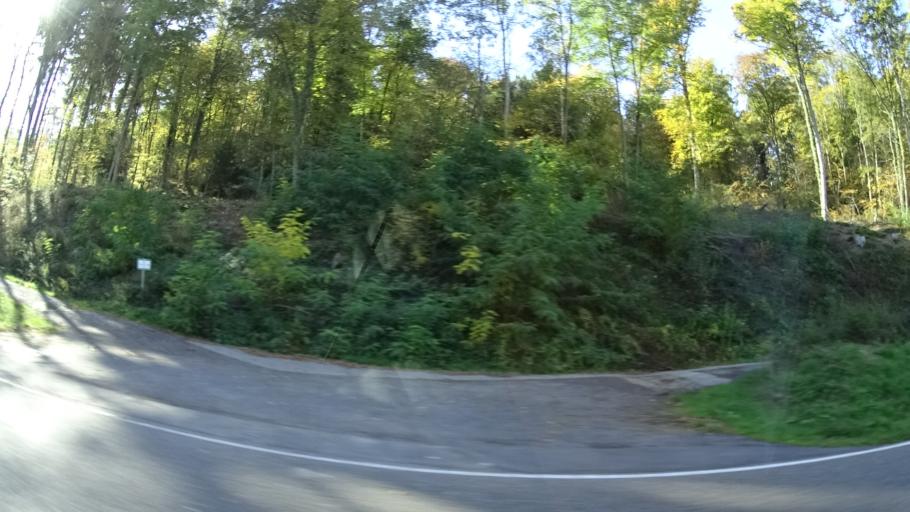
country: DE
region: Baden-Wuerttemberg
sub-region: Karlsruhe Region
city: Konigsbach-Stein
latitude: 48.9563
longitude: 8.5615
